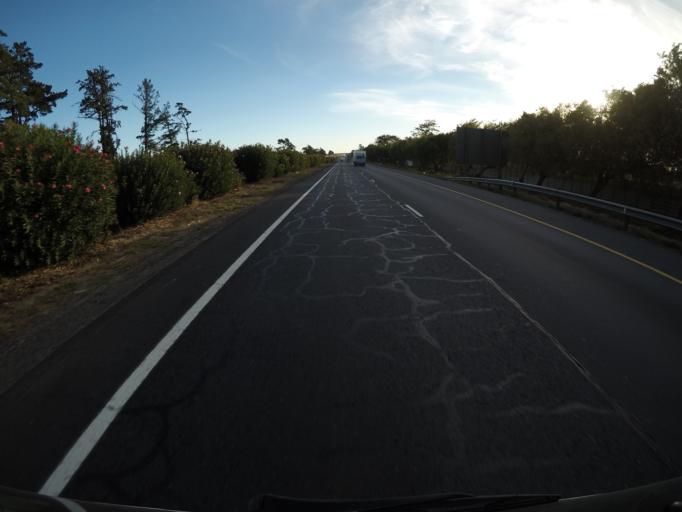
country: ZA
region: Western Cape
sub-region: City of Cape Town
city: Kraaifontein
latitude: -33.8519
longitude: 18.7048
